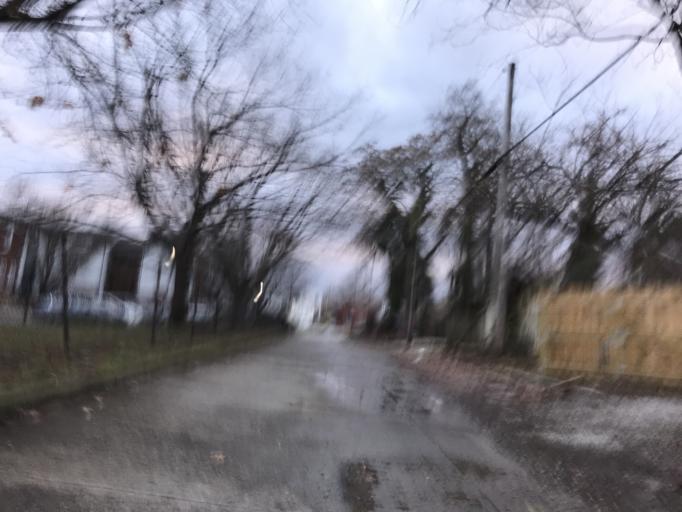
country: US
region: Kentucky
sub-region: Jefferson County
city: Louisville
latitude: 38.2474
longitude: -85.7382
